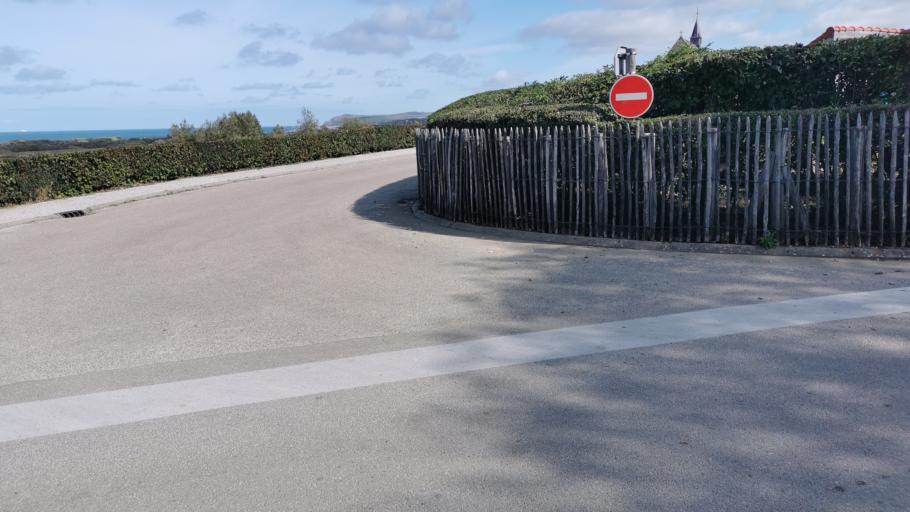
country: FR
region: Nord-Pas-de-Calais
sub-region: Departement du Pas-de-Calais
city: Wissant
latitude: 50.8666
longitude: 1.6292
